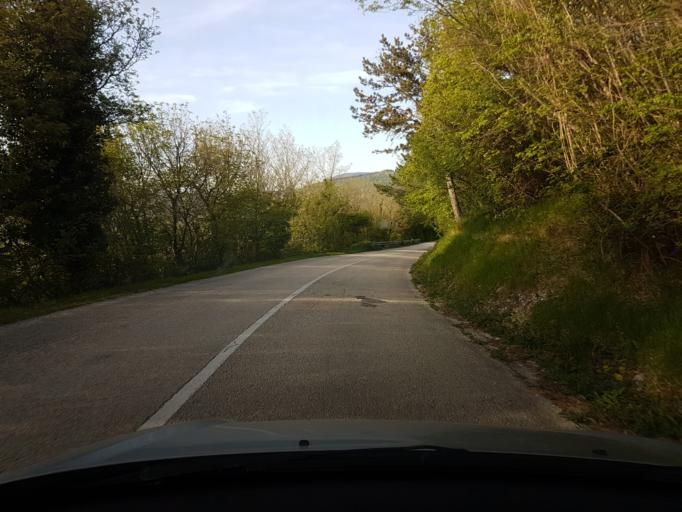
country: IT
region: Friuli Venezia Giulia
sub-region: Provincia di Trieste
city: Dolina
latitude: 45.5892
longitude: 13.8524
